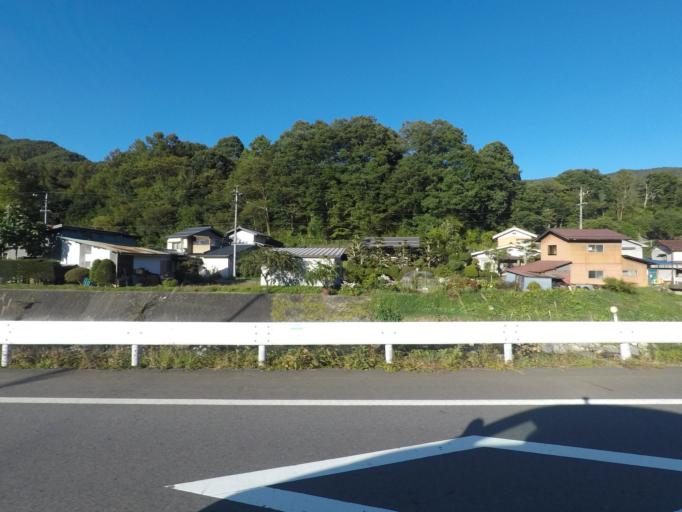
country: JP
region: Nagano
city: Tatsuno
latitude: 35.9689
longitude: 137.7607
